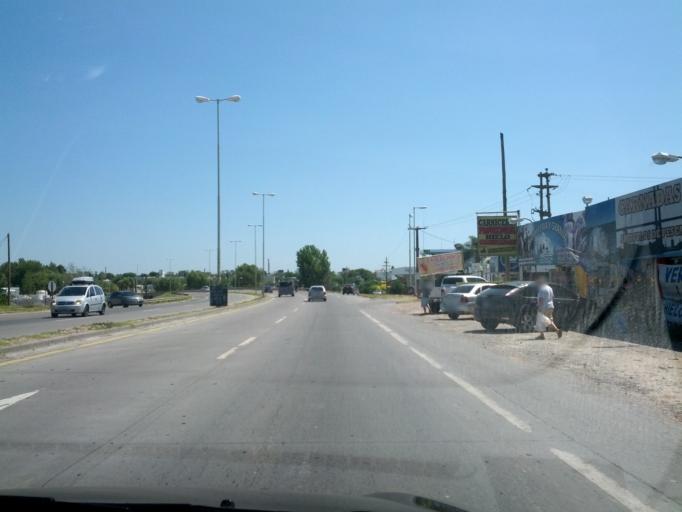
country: AR
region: Buenos Aires
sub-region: Partido de Campana
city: Campana
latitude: -34.1726
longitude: -58.9716
